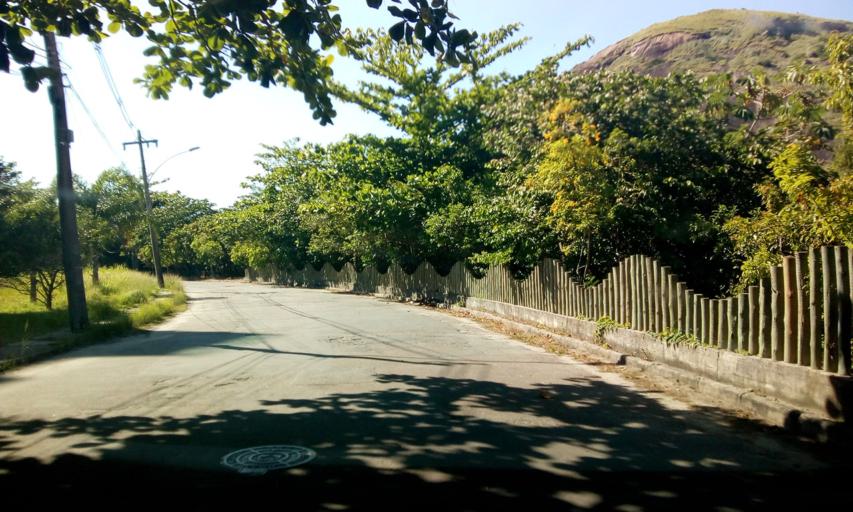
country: BR
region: Rio de Janeiro
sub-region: Nilopolis
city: Nilopolis
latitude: -23.0251
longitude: -43.4882
